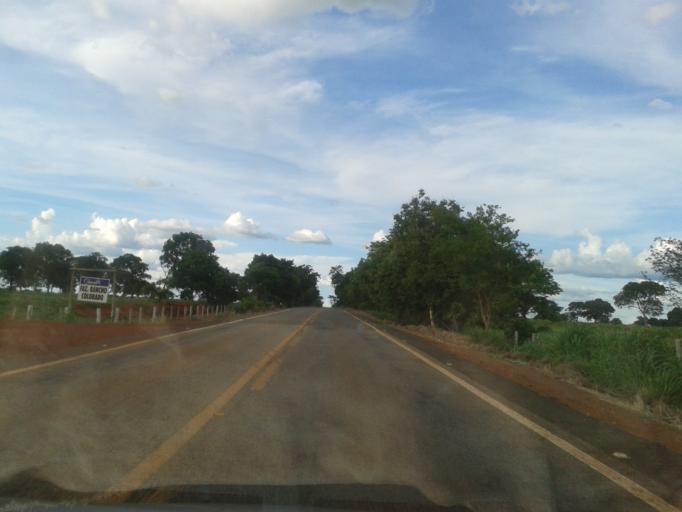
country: BR
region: Goias
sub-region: Crixas
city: Crixas
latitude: -14.0780
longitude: -50.3329
